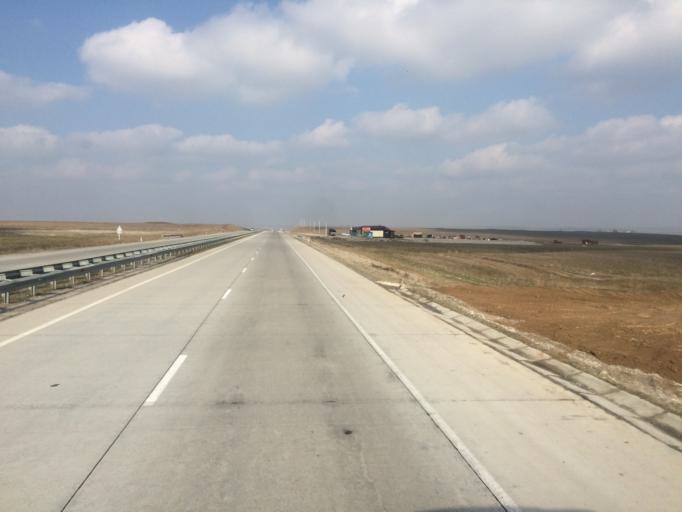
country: KZ
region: Ongtustik Qazaqstan
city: Temirlanovka
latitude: 42.5667
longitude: 69.3109
